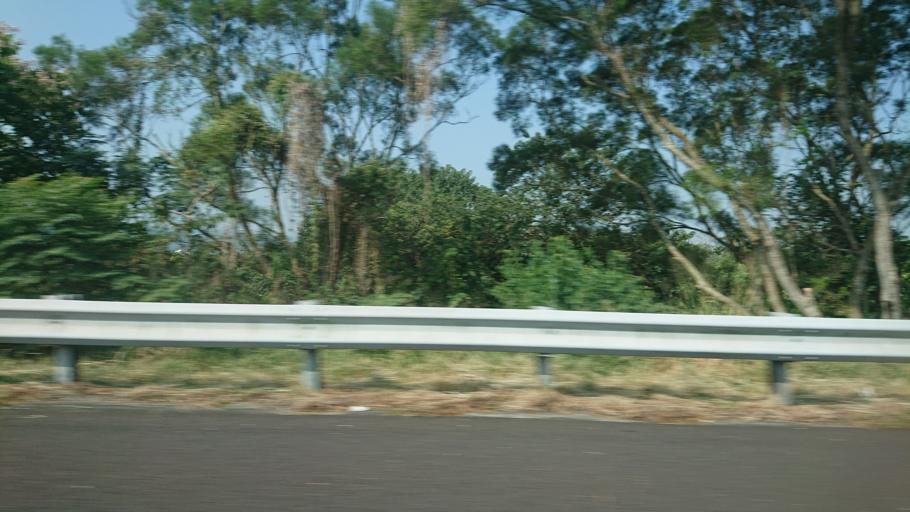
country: TW
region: Taiwan
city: Lugu
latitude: 23.8253
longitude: 120.7076
